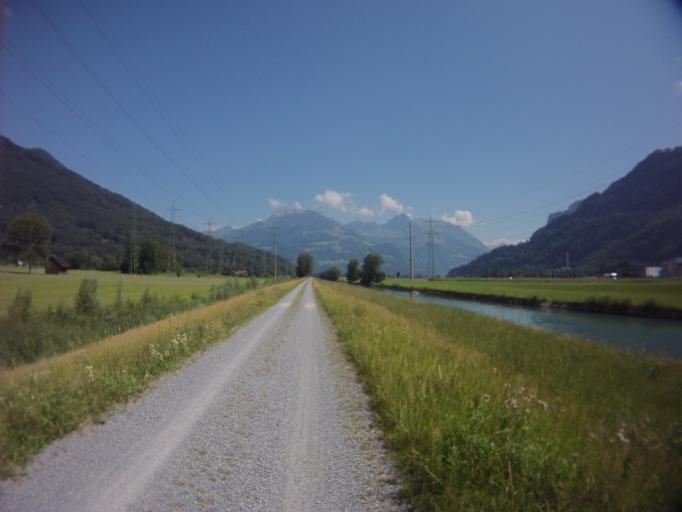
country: CH
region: Glarus
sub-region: Glarus
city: Bilten
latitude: 47.1520
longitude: 9.0368
